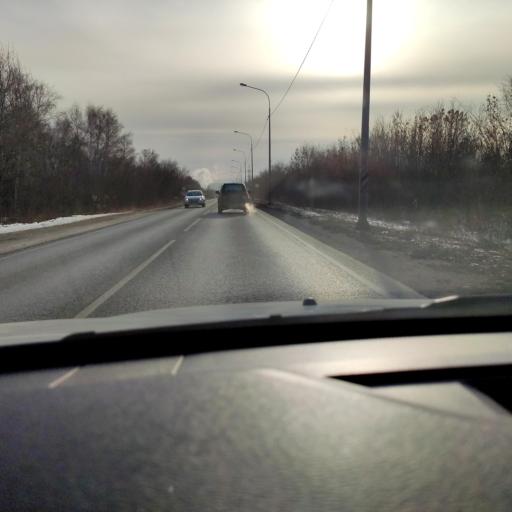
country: RU
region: Samara
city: Petra-Dubrava
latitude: 53.2800
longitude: 50.3787
